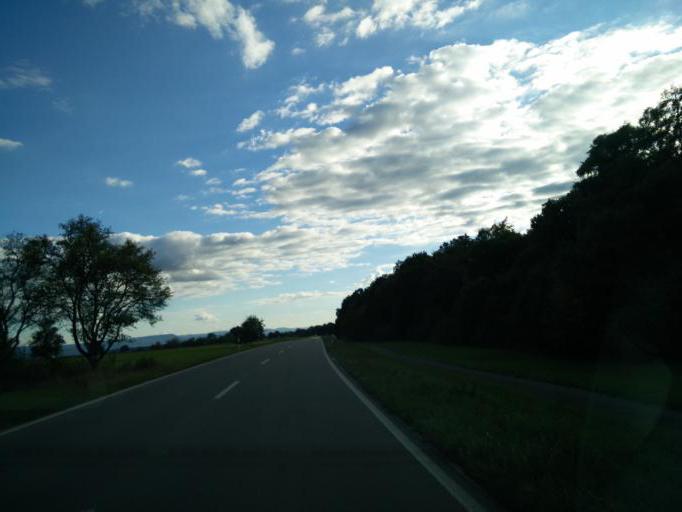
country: DE
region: Baden-Wuerttemberg
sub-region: Tuebingen Region
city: Kusterdingen
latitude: 48.5632
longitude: 9.1021
